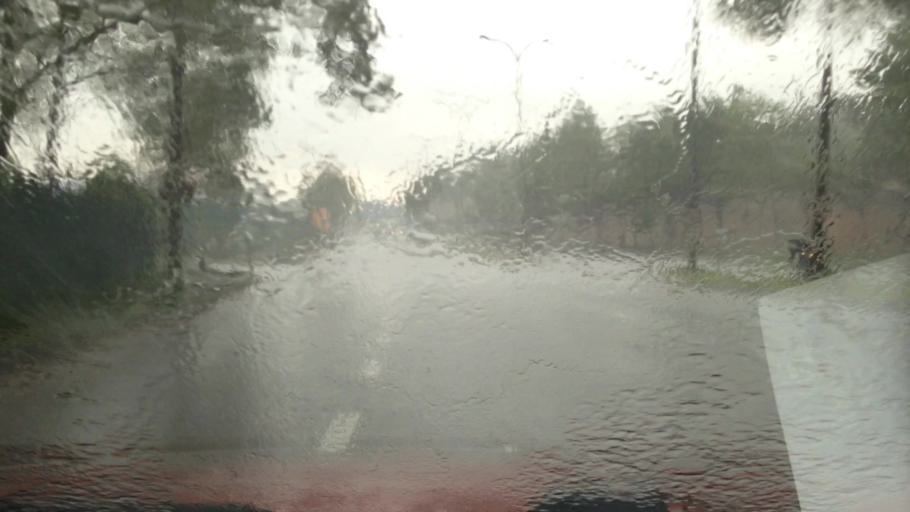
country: MY
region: Selangor
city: Subang Jaya
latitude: 3.0289
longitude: 101.5892
